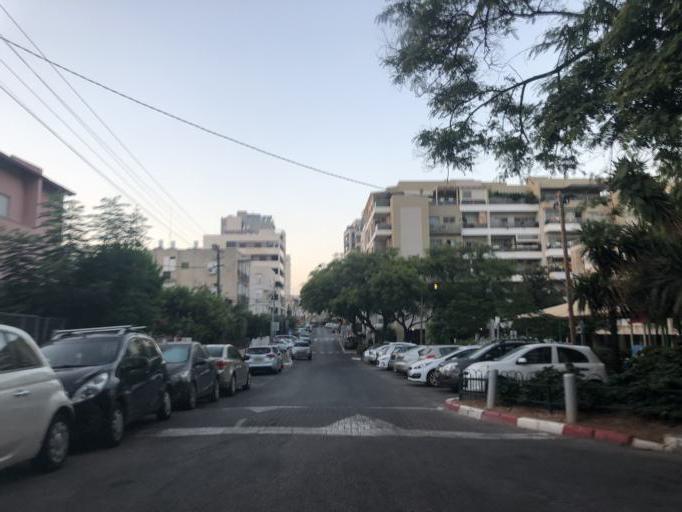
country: IL
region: Tel Aviv
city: Bene Beraq
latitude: 32.0661
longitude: 34.8273
